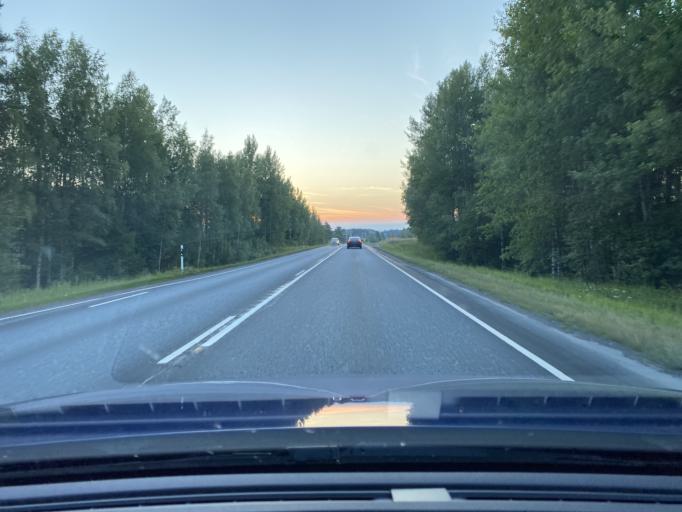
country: FI
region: Pirkanmaa
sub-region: Luoteis-Pirkanmaa
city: Ikaalinen
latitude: 61.8032
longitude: 22.9694
